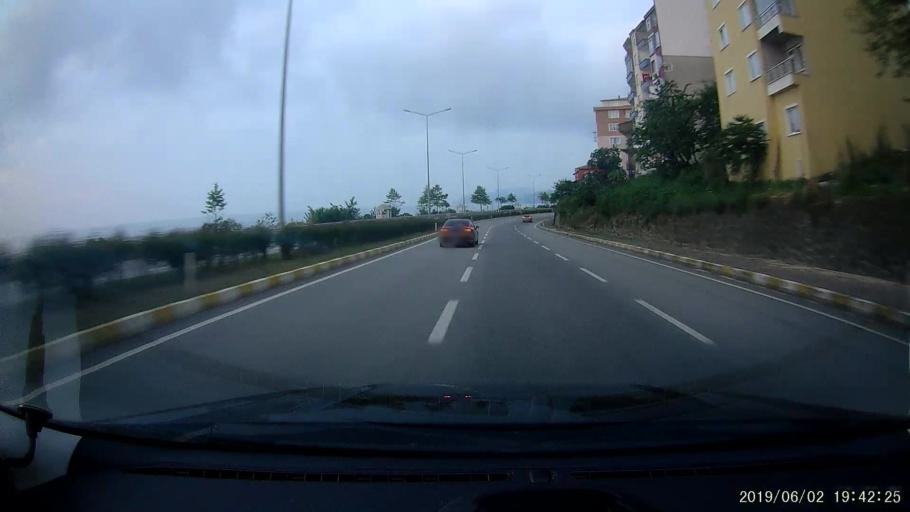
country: TR
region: Giresun
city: Kesap
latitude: 40.9169
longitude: 38.5044
